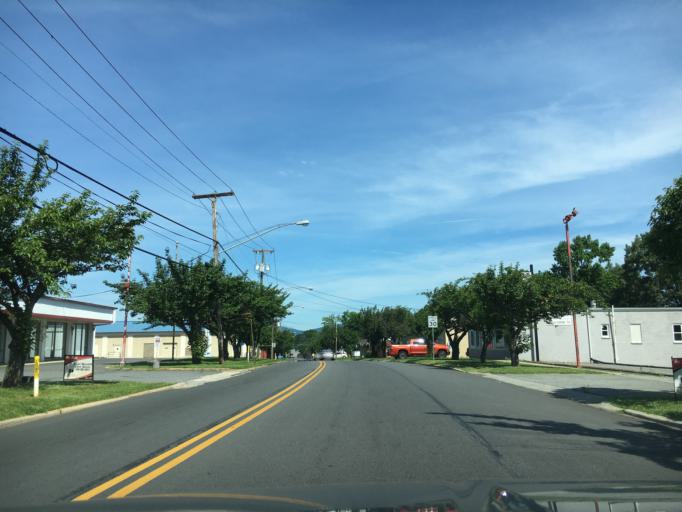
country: US
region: Virginia
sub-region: City of Lynchburg
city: West Lynchburg
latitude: 37.4007
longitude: -79.1740
